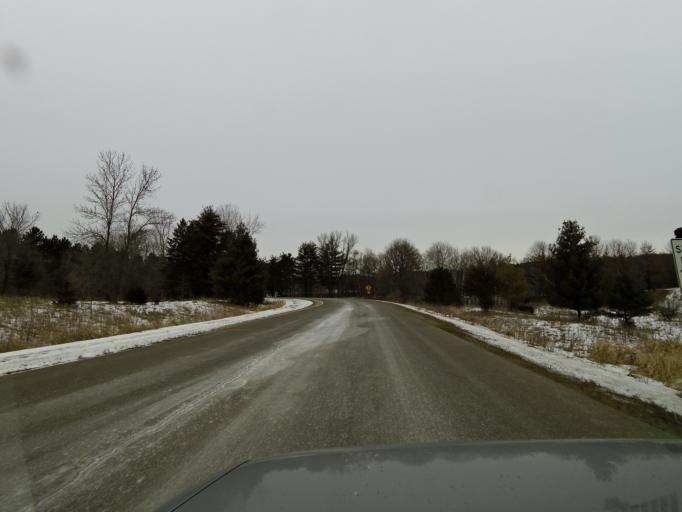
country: US
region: Minnesota
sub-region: Washington County
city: Lake Elmo
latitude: 44.9720
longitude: -92.9034
